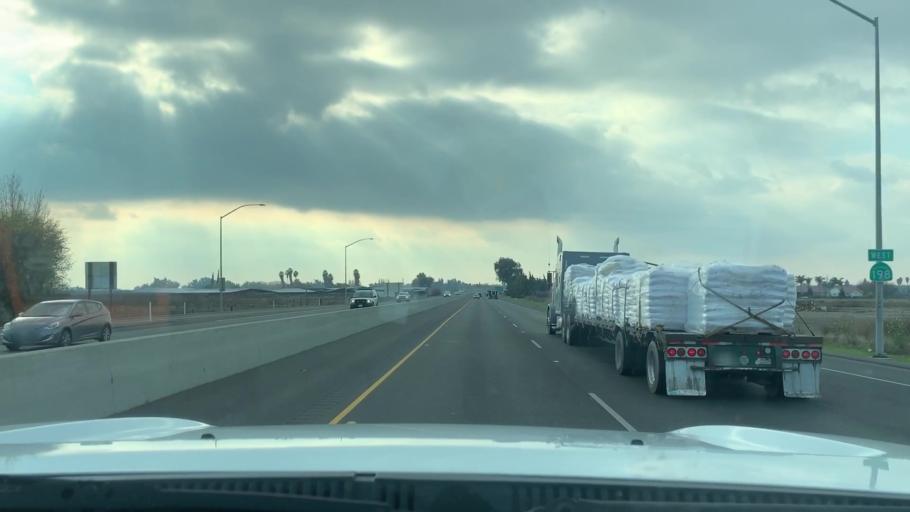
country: US
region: California
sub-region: Kings County
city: Lemoore
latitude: 36.2964
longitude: -119.7580
